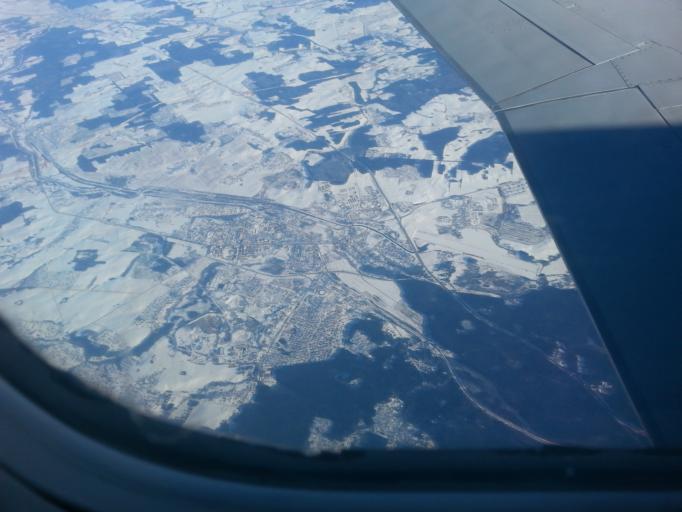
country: BY
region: Minsk
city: Novosel'ye
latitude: 53.9412
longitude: 27.2484
